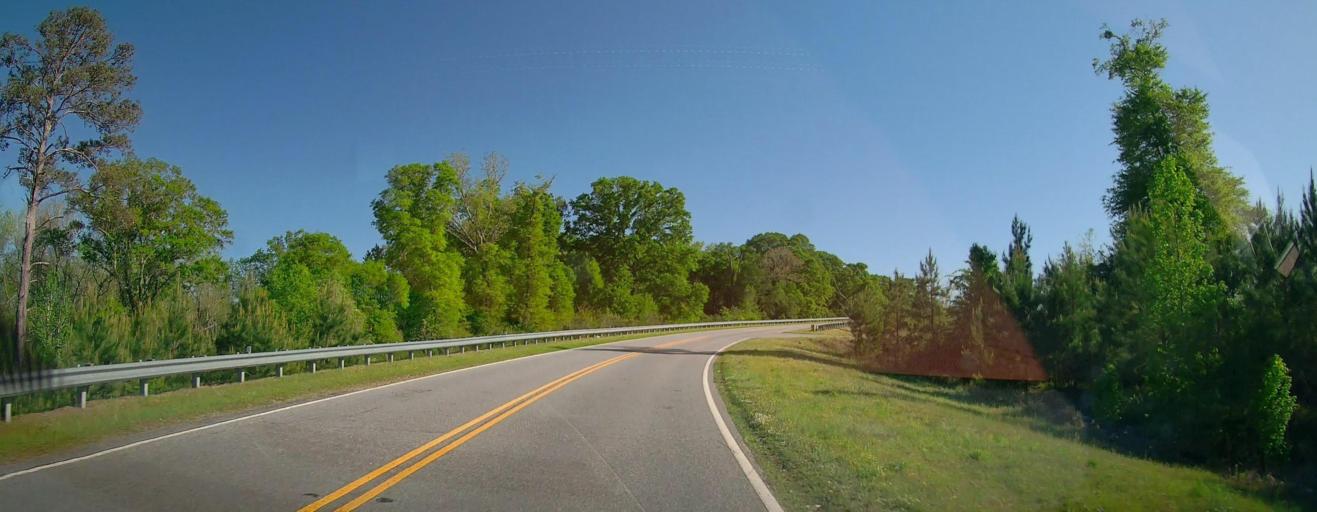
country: US
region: Georgia
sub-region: Houston County
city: Perry
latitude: 32.4414
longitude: -83.7260
